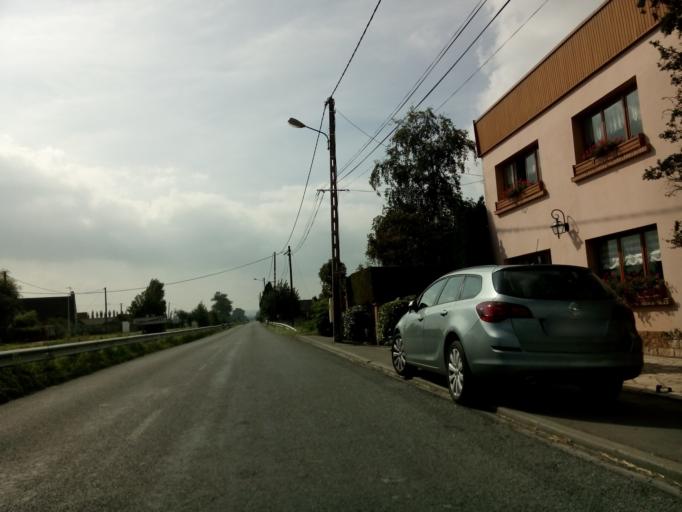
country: FR
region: Nord-Pas-de-Calais
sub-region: Departement du Pas-de-Calais
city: Ardres
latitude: 50.8916
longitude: 1.9684
